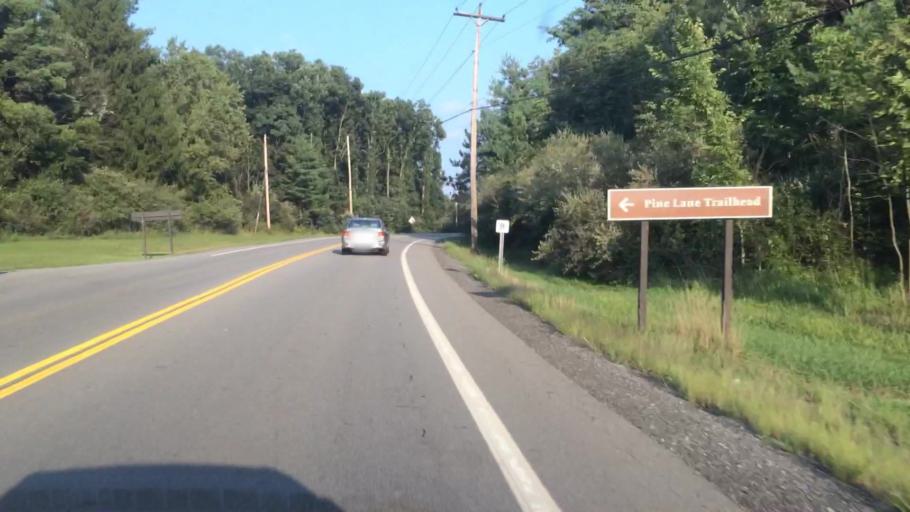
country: US
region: Ohio
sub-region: Summit County
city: Peninsula
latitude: 41.2389
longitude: -81.5387
